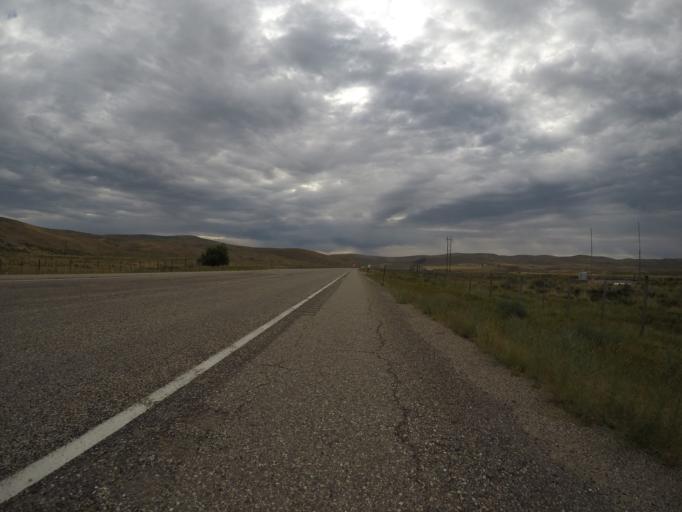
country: US
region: Utah
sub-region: Rich County
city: Randolph
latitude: 41.8240
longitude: -110.9039
